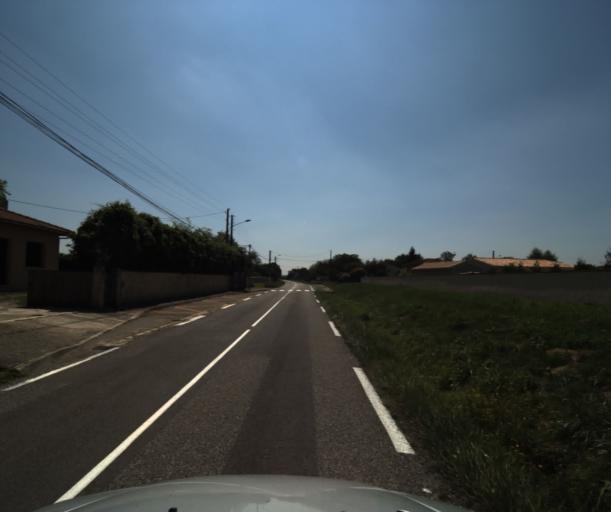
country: FR
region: Midi-Pyrenees
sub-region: Departement de la Haute-Garonne
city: Labastidette
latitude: 43.4400
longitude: 1.2581
